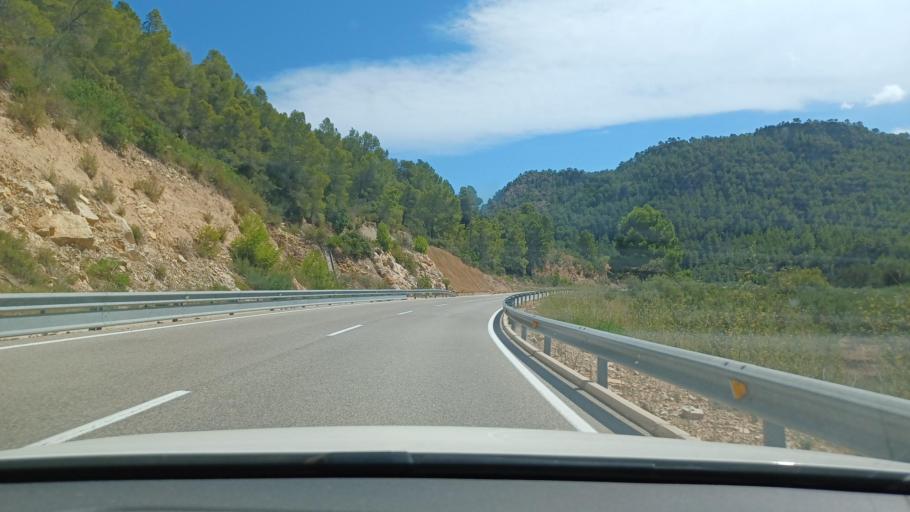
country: ES
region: Catalonia
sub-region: Provincia de Tarragona
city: Bot
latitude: 40.9737
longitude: 0.4279
